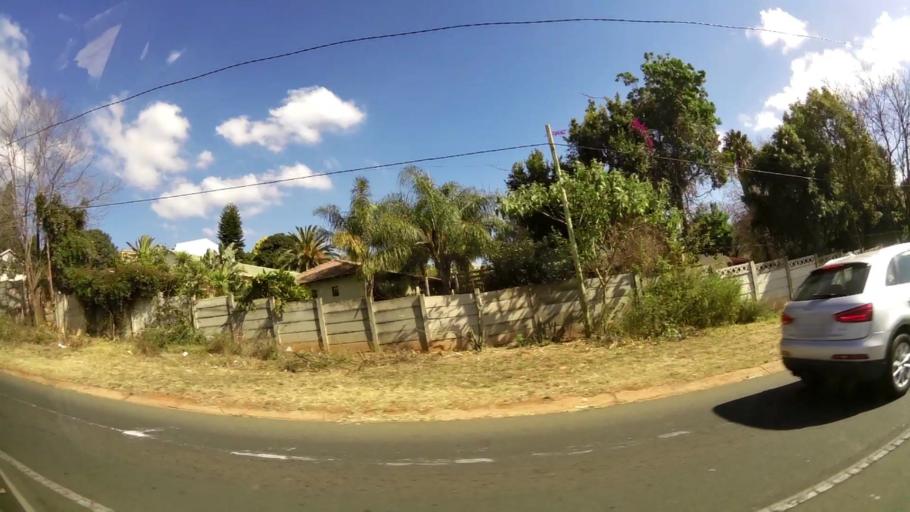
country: ZA
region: Gauteng
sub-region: City of Johannesburg Metropolitan Municipality
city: Roodepoort
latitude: -26.1099
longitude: 27.8384
